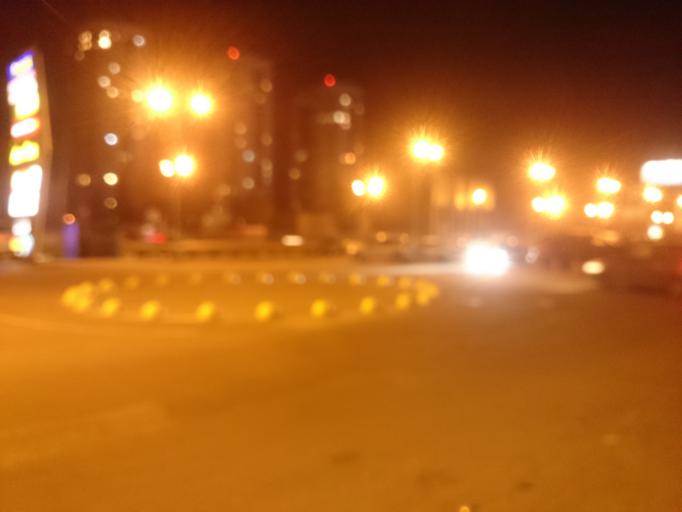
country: RU
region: Moskovskaya
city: Balashikha
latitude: 55.7982
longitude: 37.9849
